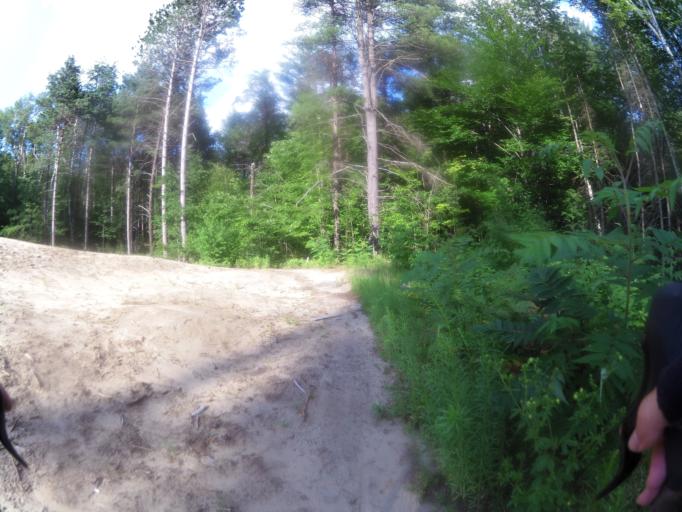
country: CA
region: Ontario
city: Ottawa
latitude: 45.3220
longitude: -75.7266
